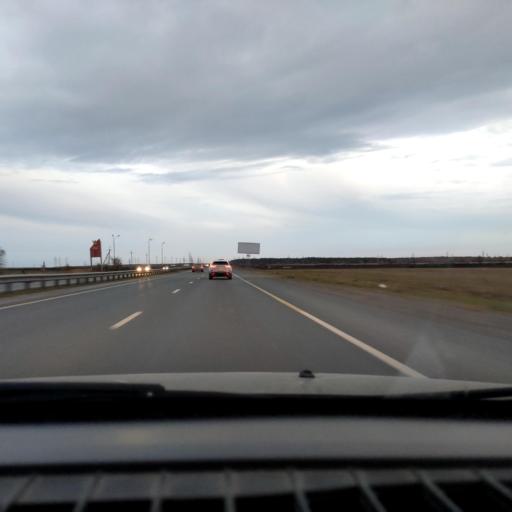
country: RU
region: Samara
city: Zhigulevsk
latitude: 53.5554
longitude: 49.5034
